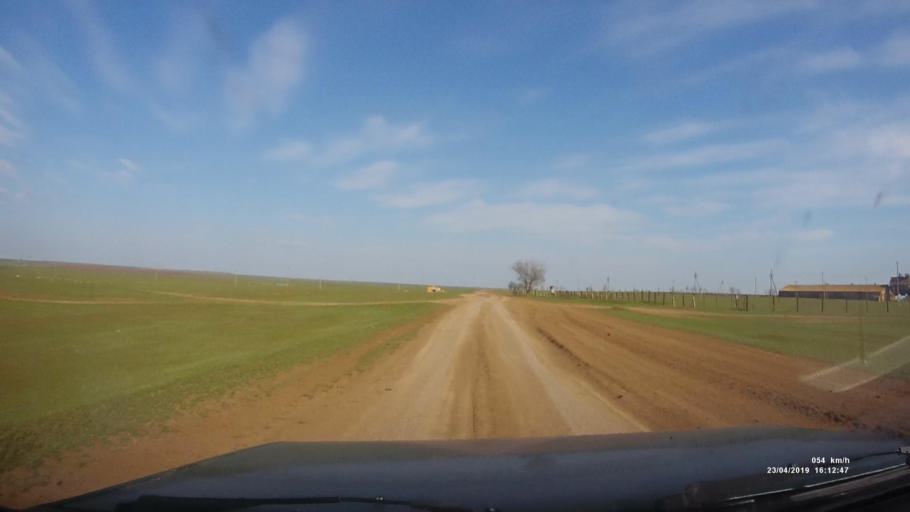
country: RU
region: Kalmykiya
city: Priyutnoye
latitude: 46.4651
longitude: 43.1299
